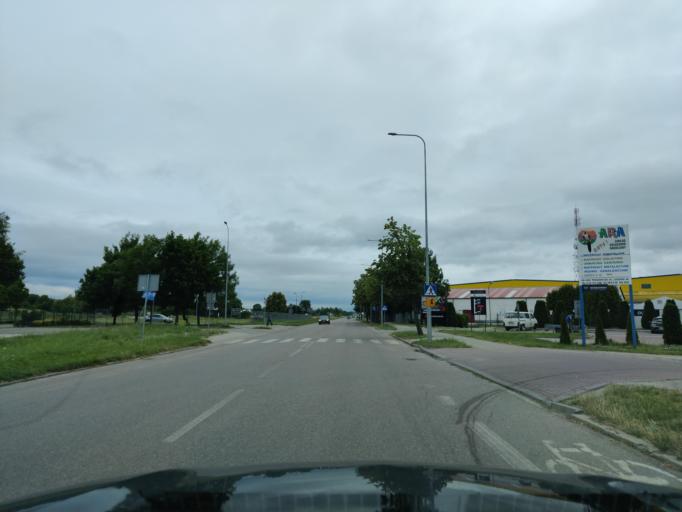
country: PL
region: Masovian Voivodeship
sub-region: Powiat przasnyski
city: Przasnysz
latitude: 53.0093
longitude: 20.8913
